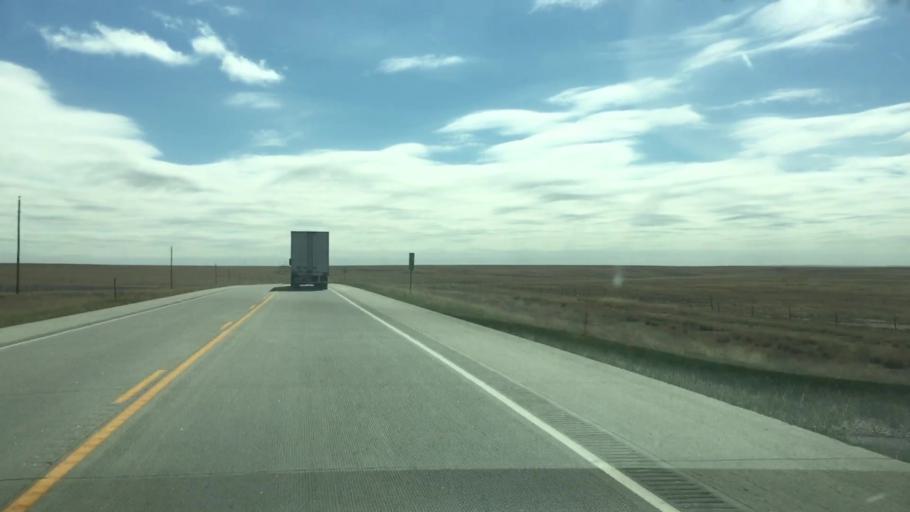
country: US
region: Colorado
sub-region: Lincoln County
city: Hugo
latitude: 39.0184
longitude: -103.3087
